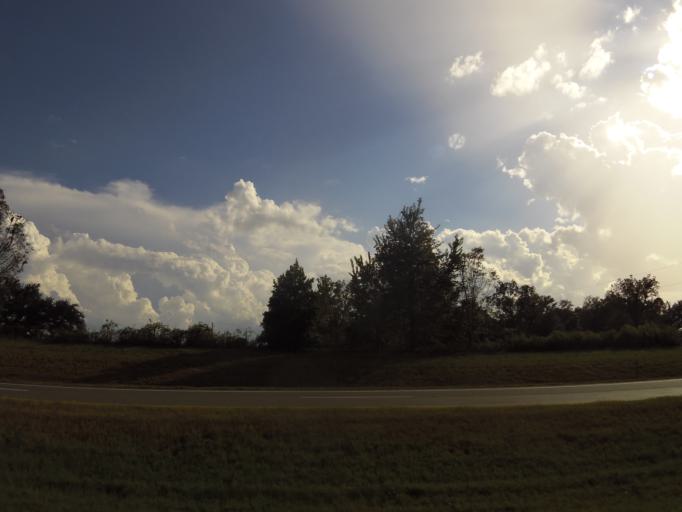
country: US
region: Georgia
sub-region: Brooks County
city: Quitman
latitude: 30.7881
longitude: -83.6348
